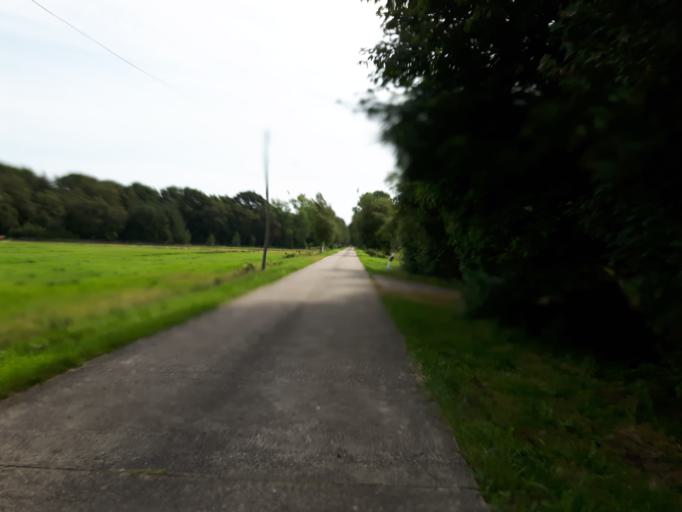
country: DE
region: Lower Saxony
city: Ovelgonne
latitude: 53.2975
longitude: 8.3168
